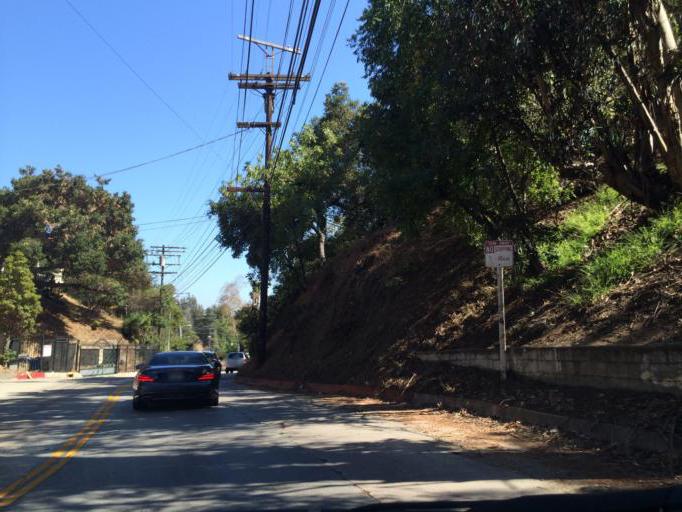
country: US
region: California
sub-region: Los Angeles County
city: Universal City
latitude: 34.1183
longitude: -118.3758
